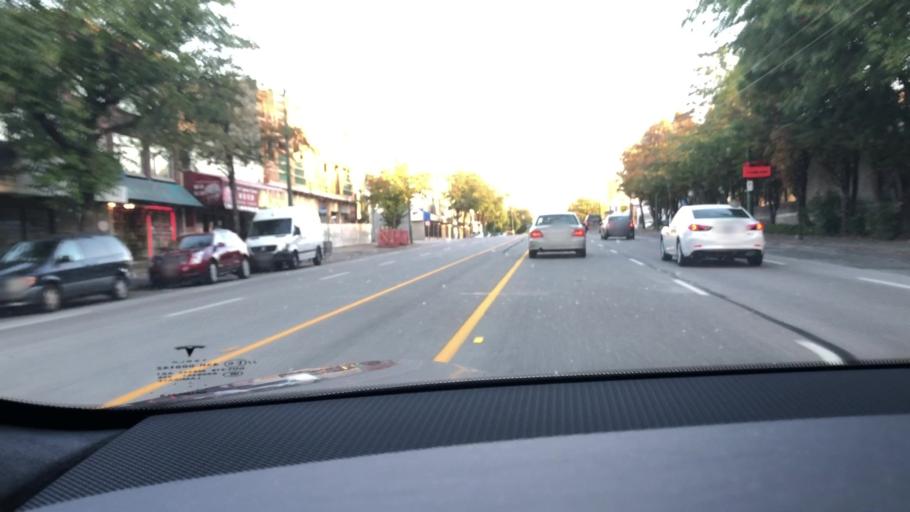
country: CA
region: British Columbia
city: Vancouver
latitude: 49.2543
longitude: -123.0845
